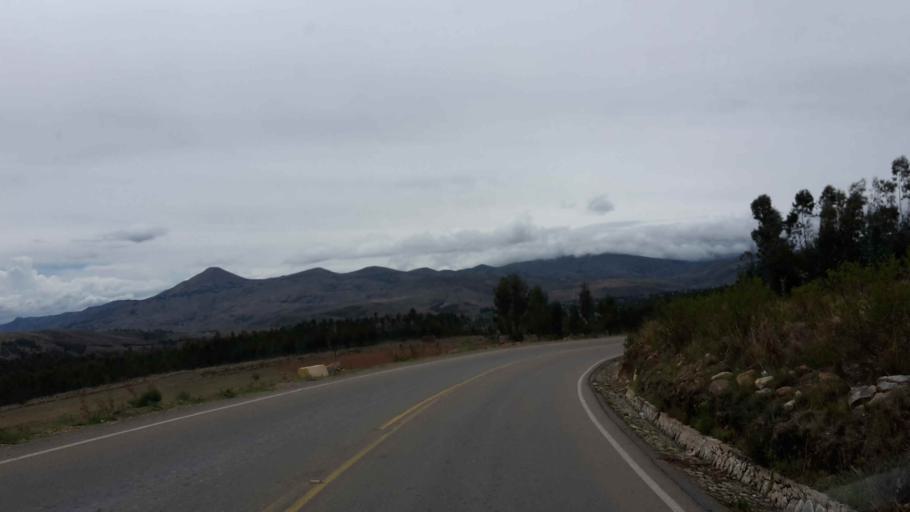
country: BO
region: Cochabamba
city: Arani
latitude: -17.4656
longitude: -65.6960
